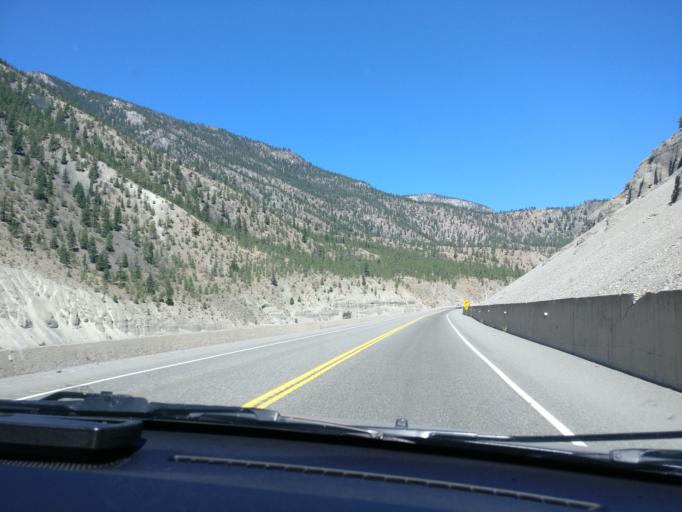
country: CA
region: British Columbia
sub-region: Thompson-Nicola Regional District
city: Ashcroft
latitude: 50.2772
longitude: -121.4052
